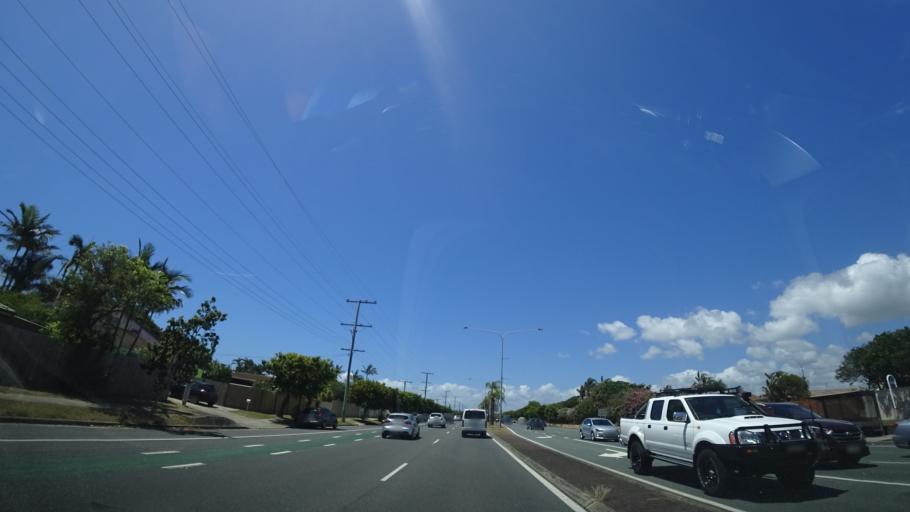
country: AU
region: Queensland
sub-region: Sunshine Coast
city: Mooloolaba
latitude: -26.7145
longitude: 153.1300
